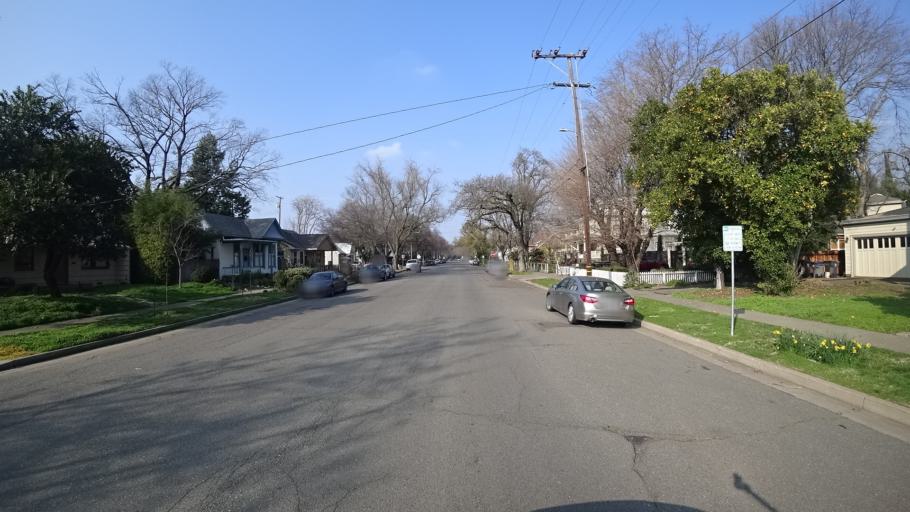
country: US
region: California
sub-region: Yolo County
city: Davis
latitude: 38.5459
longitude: -121.7372
